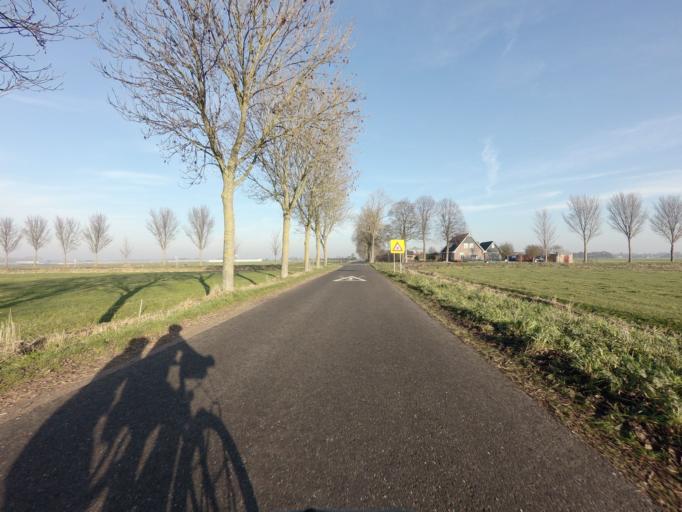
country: NL
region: Utrecht
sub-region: Gemeente De Ronde Venen
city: Mijdrecht
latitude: 52.2008
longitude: 4.8288
